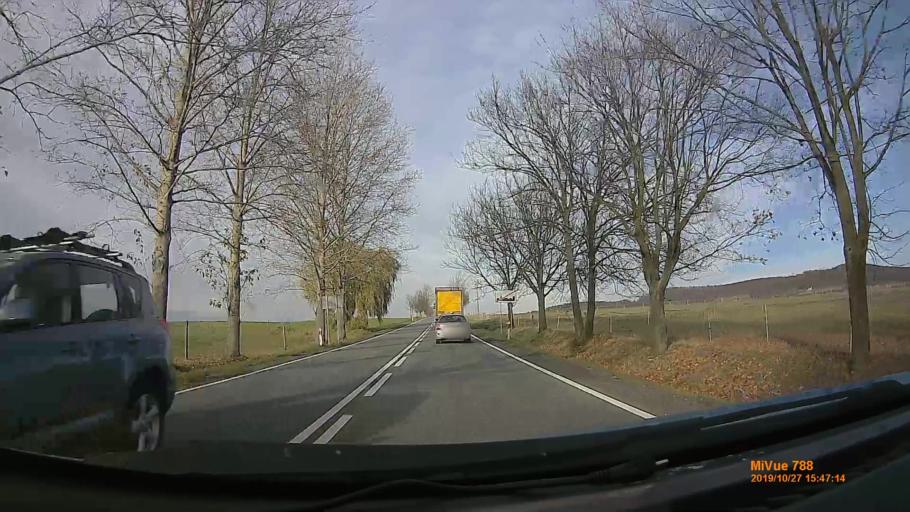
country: PL
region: Lower Silesian Voivodeship
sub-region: Powiat klodzki
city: Bozkow
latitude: 50.4879
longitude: 16.5845
